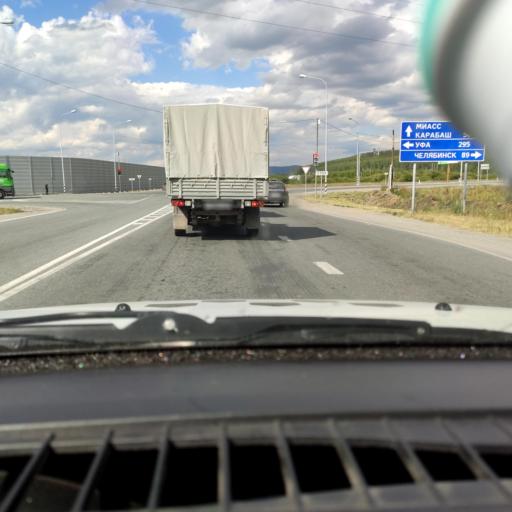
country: RU
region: Chelyabinsk
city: Miass
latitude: 54.9436
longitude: 60.0506
